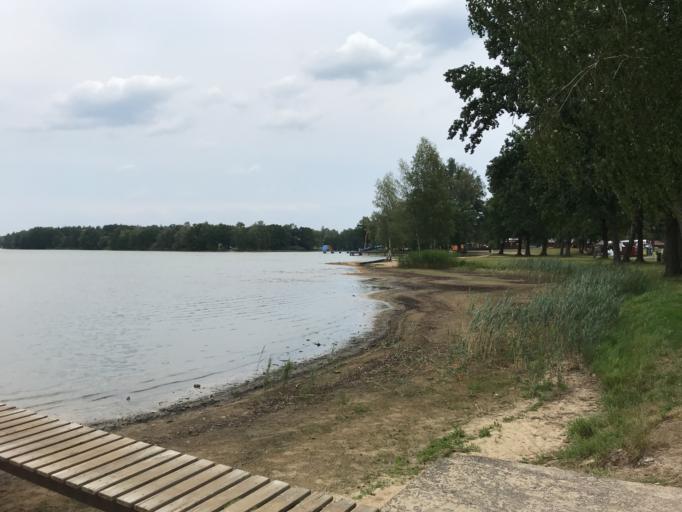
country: CZ
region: Jihocesky
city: Chlum u Trebone
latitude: 48.9593
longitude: 14.9396
